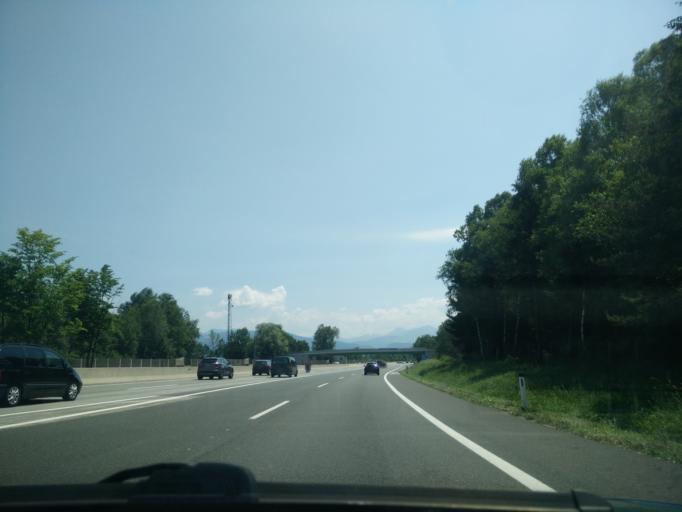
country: AT
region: Salzburg
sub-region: Politischer Bezirk Salzburg-Umgebung
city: Grodig
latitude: 47.7687
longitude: 12.9865
